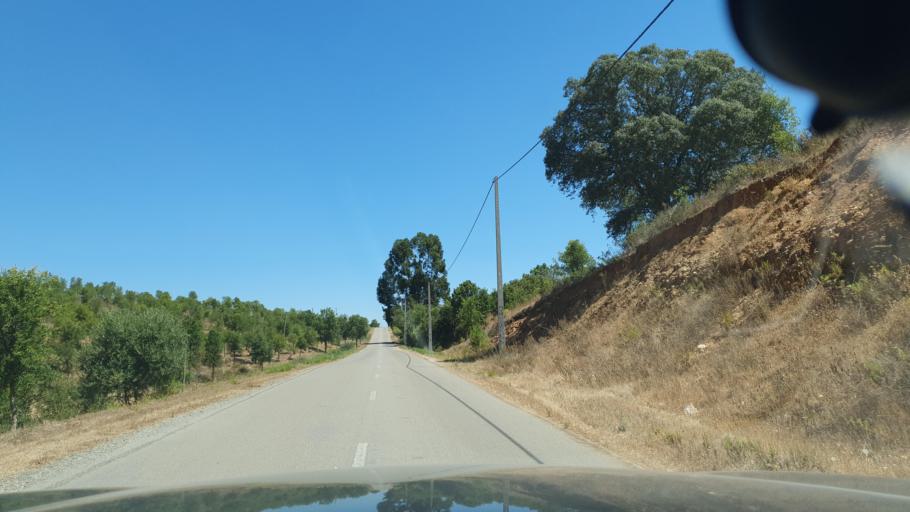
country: PT
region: Beja
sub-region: Odemira
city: Odemira
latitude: 37.5473
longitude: -8.4587
